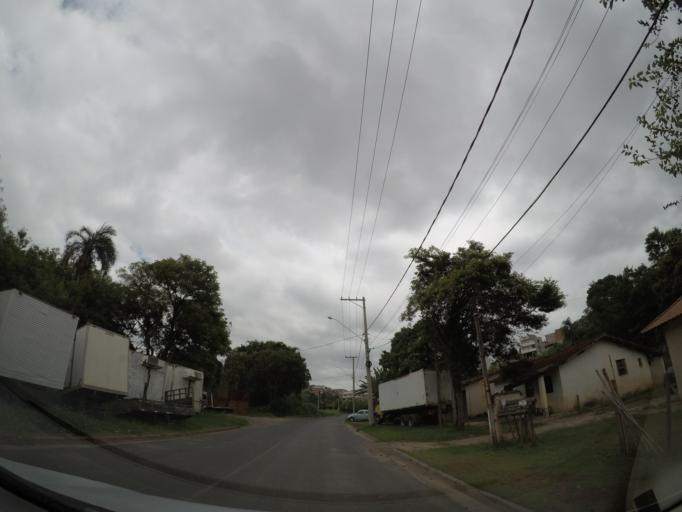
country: BR
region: Sao Paulo
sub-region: Louveira
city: Louveira
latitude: -23.0929
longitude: -46.9838
